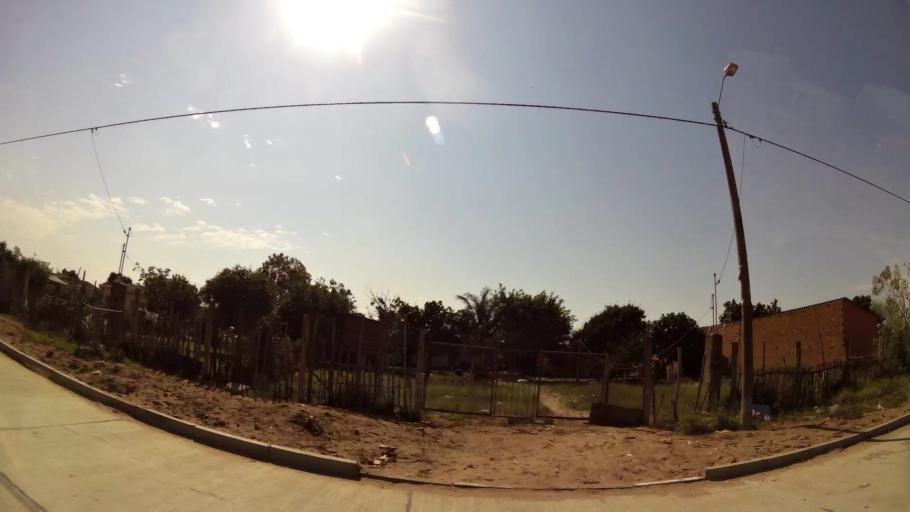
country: BO
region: Santa Cruz
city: Cotoca
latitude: -17.7512
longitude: -63.0930
